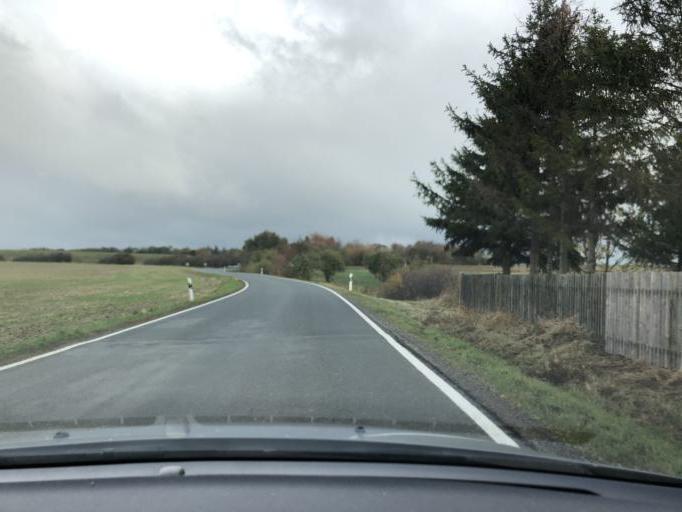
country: DE
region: Thuringia
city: Anrode
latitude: 51.2570
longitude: 10.3495
